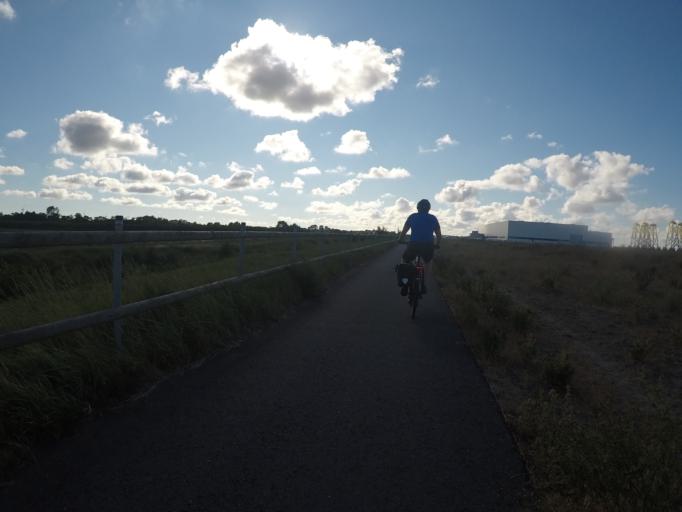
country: DE
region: Lower Saxony
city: Cuxhaven
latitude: 53.8369
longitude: 8.7624
